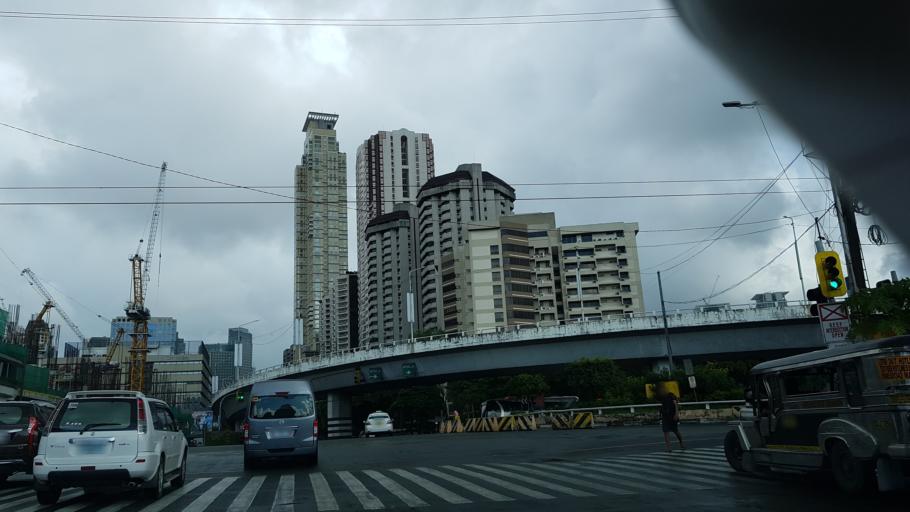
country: PH
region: Metro Manila
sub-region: Makati City
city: Makati City
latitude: 14.5499
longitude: 121.0298
